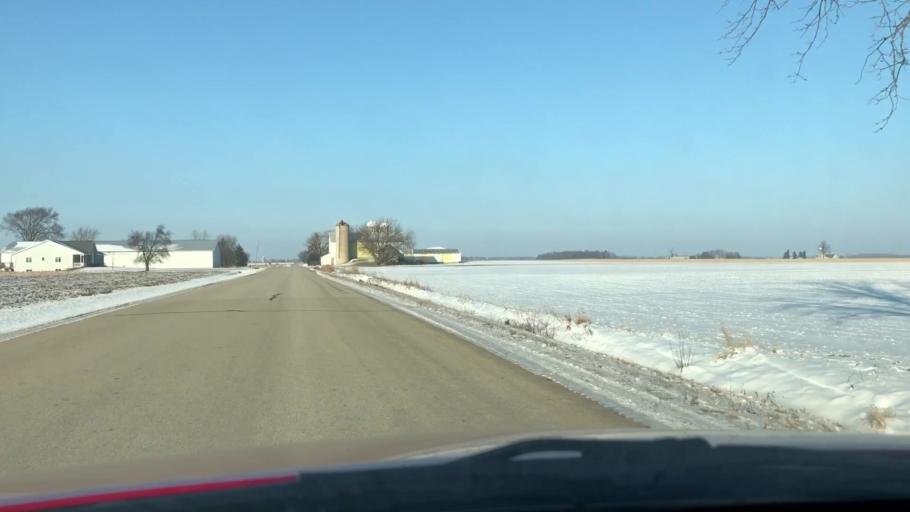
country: US
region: Wisconsin
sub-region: Outagamie County
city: Seymour
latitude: 44.4880
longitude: -88.3090
